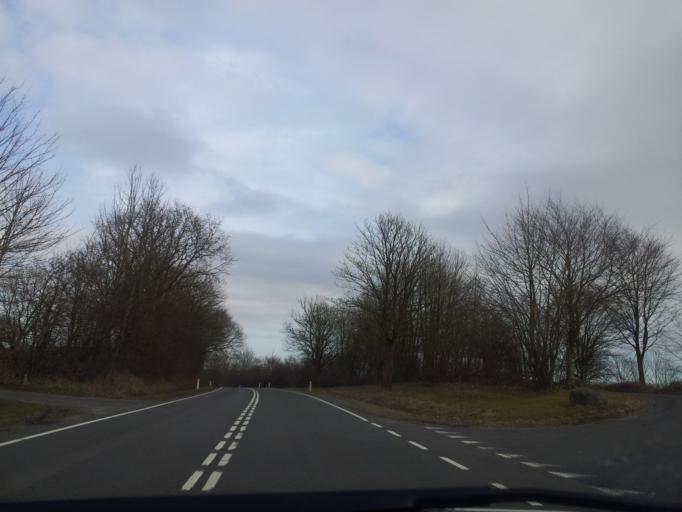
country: DK
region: South Denmark
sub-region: Vejen Kommune
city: Brorup
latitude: 55.4399
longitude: 9.0680
